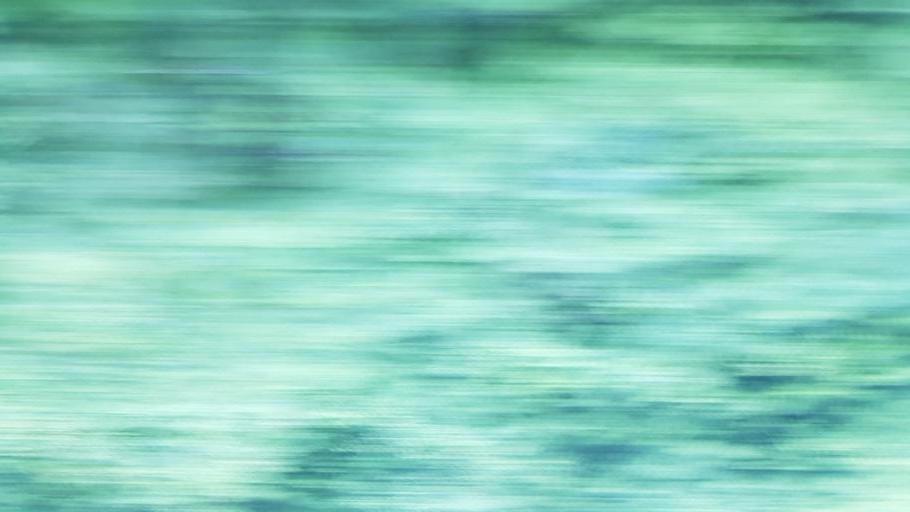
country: NO
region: Sor-Trondelag
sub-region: Melhus
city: Lundamo
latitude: 63.2173
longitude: 10.2952
